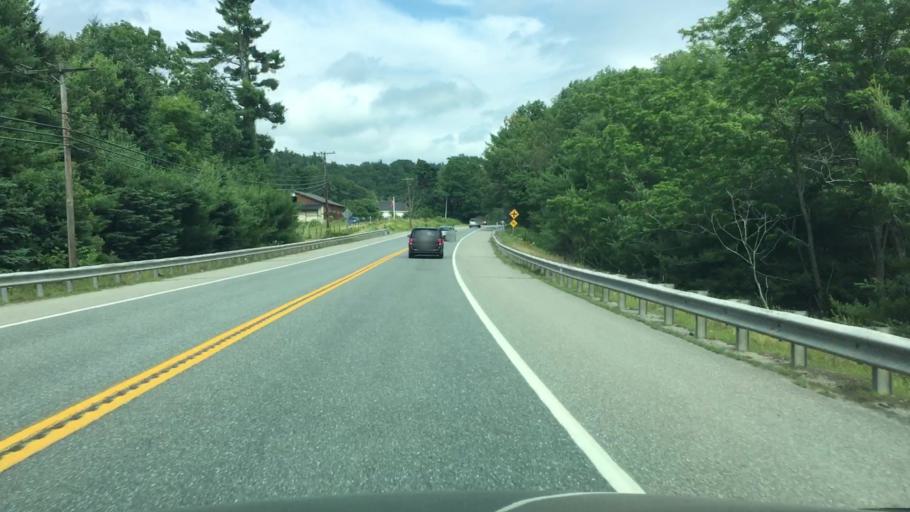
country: US
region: Maine
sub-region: Hancock County
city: Orland
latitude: 44.5667
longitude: -68.6831
